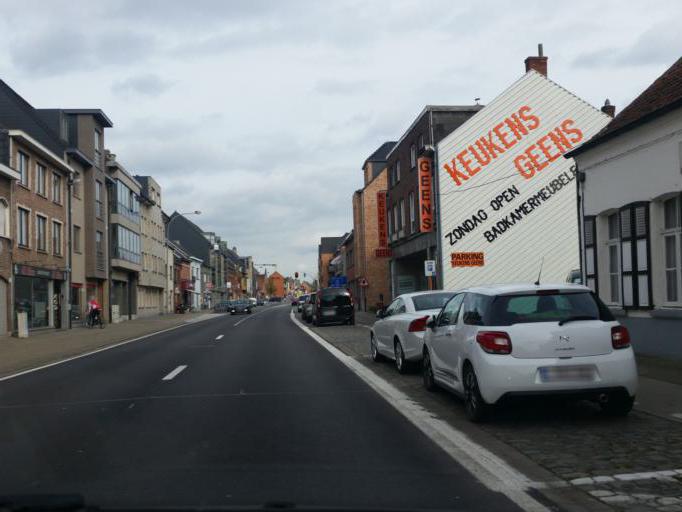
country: BE
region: Flanders
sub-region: Provincie Antwerpen
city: Putte
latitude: 51.0536
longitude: 4.6264
